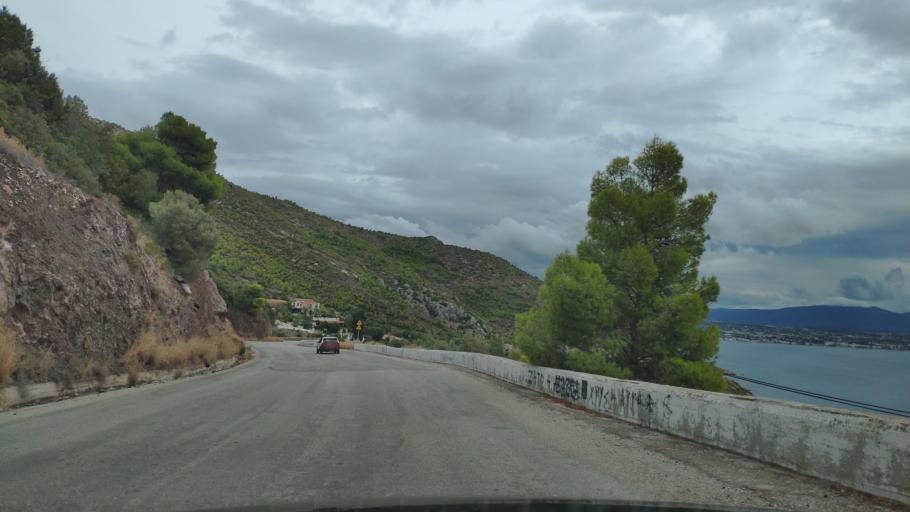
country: GR
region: Peloponnese
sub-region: Nomos Korinthias
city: Perachora
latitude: 38.0012
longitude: 22.9425
